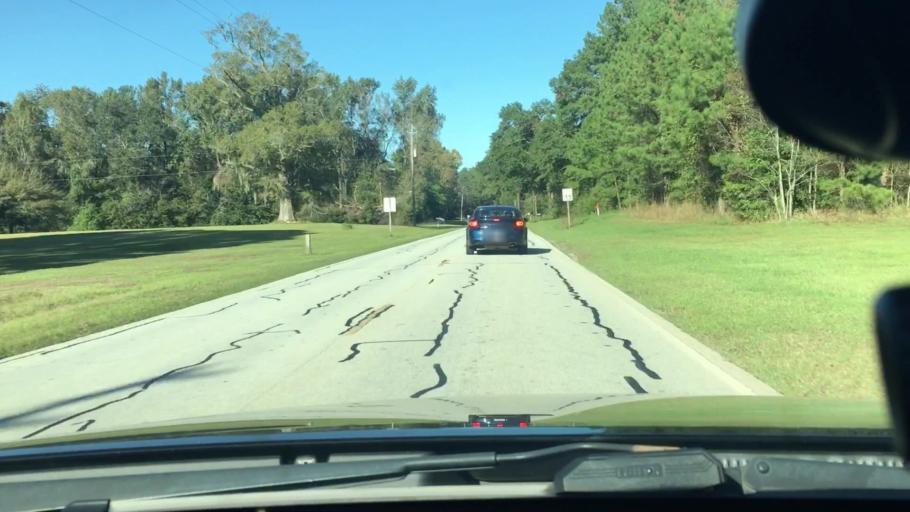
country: US
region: North Carolina
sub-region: Craven County
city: Vanceboro
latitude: 35.2916
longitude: -77.1524
